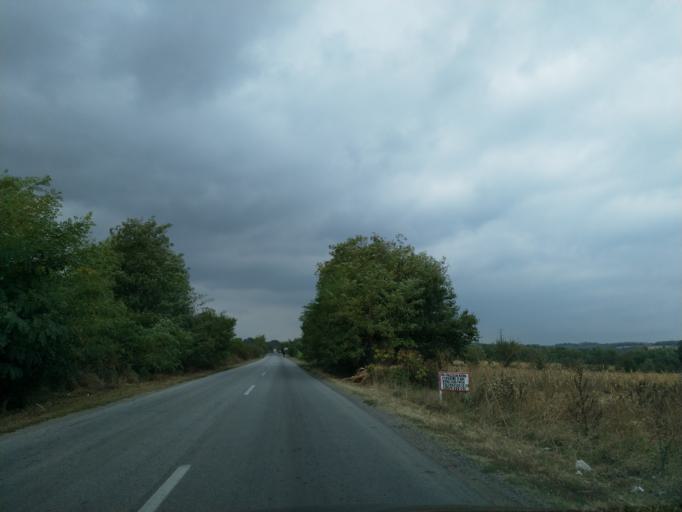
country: RS
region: Central Serbia
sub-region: Pomoravski Okrug
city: Jagodina
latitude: 43.9988
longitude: 21.2167
